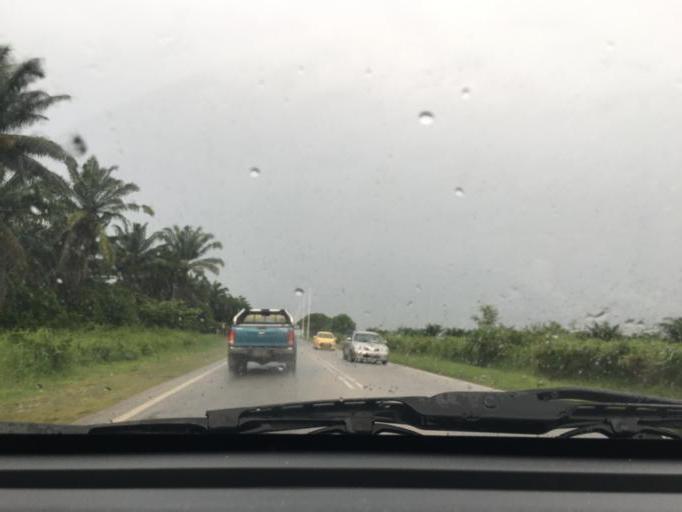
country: MY
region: Kedah
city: Sungai Petani
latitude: 5.5994
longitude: 100.6396
